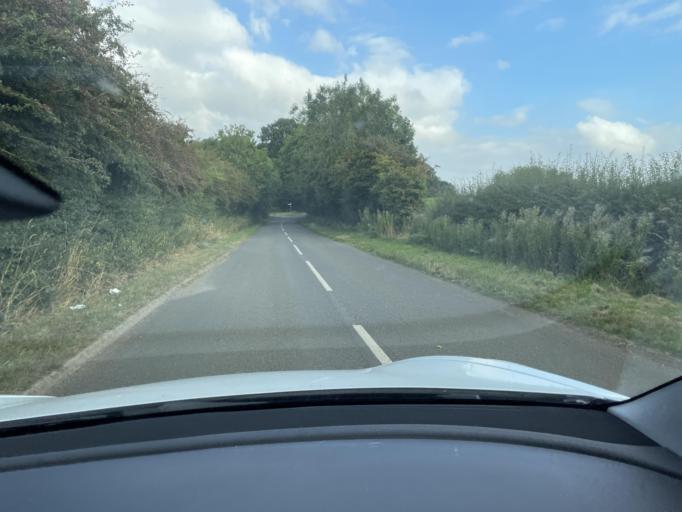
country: GB
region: England
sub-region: Leicestershire
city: Market Harborough
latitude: 52.4002
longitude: -0.9941
